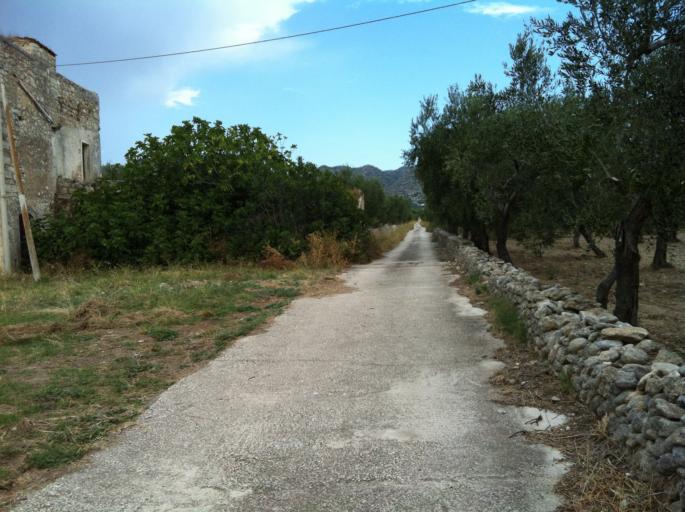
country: IT
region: Apulia
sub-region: Provincia di Foggia
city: Monte Sant'Angelo
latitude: 41.6544
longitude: 15.9559
